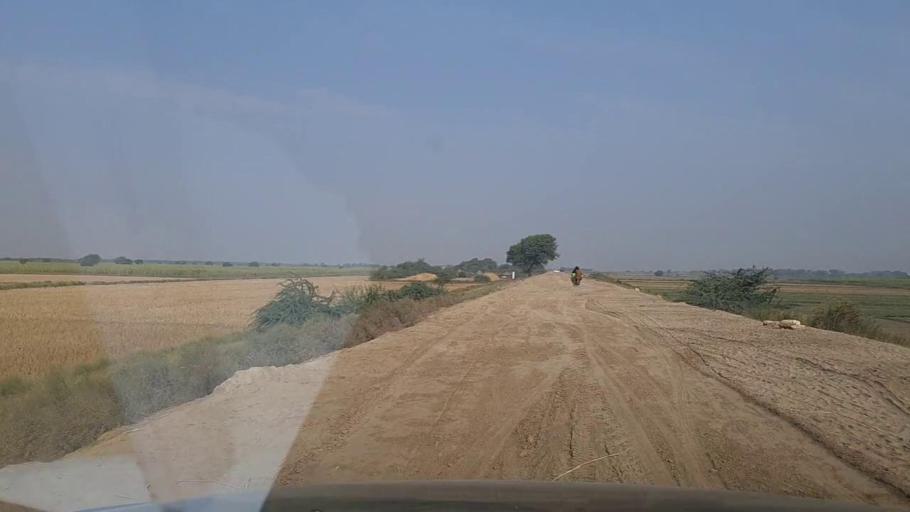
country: PK
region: Sindh
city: Bulri
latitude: 25.0090
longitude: 68.2861
